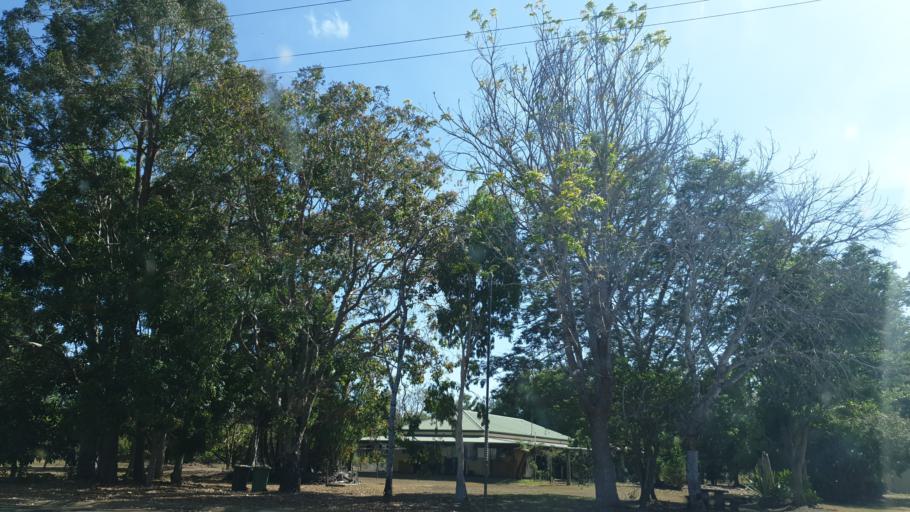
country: AU
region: Queensland
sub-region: Tablelands
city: Tolga
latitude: -17.1320
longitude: 145.4284
